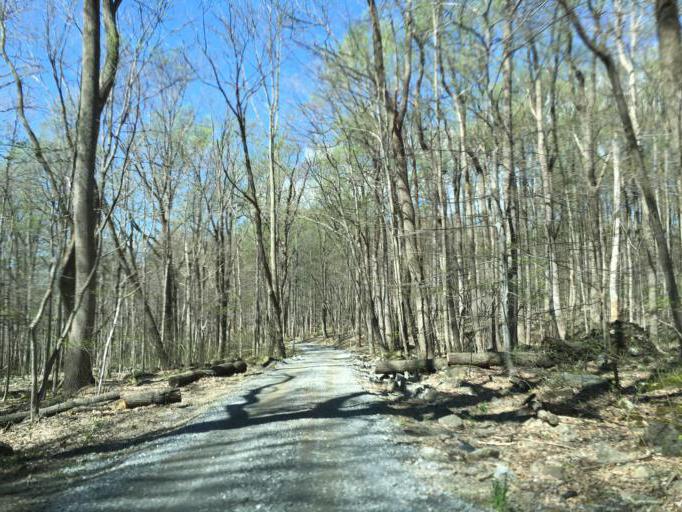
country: US
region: Maryland
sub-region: Washington County
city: Highfield-Cascade
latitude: 39.6541
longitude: -77.4775
